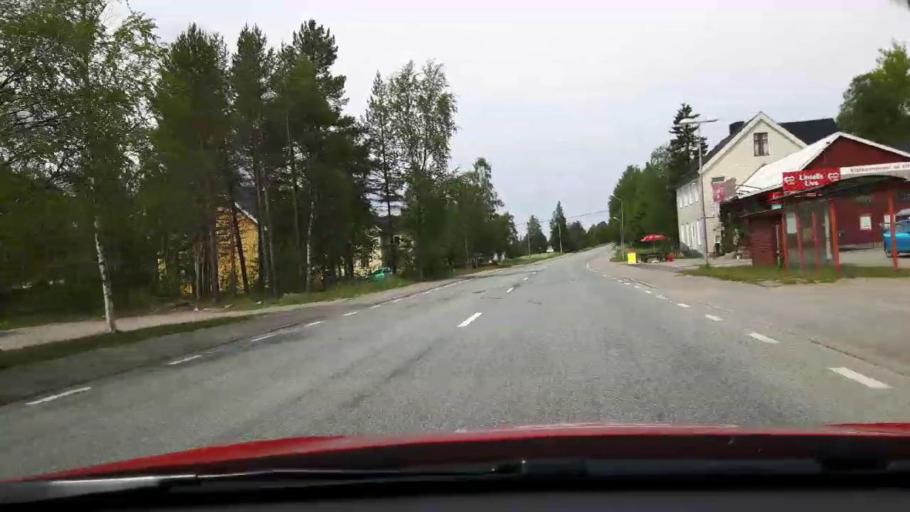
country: SE
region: Jaemtland
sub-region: Harjedalens Kommun
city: Sveg
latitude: 62.1572
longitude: 13.8899
